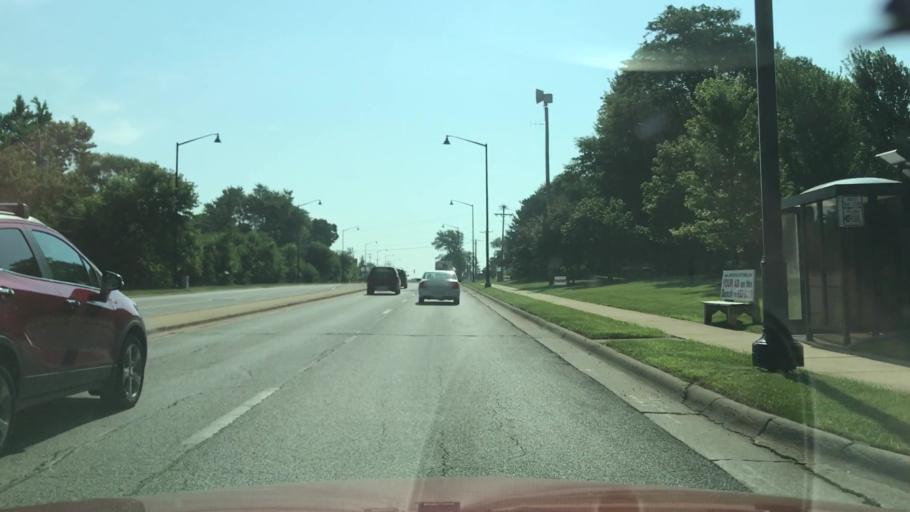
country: US
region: Illinois
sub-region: Winnebago County
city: Rockford
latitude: 42.2380
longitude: -89.0372
